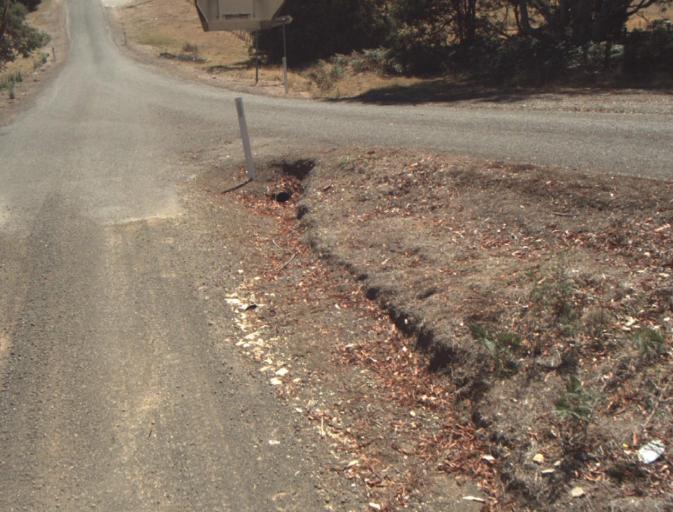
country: AU
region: Tasmania
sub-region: Dorset
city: Scottsdale
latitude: -41.2902
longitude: 147.3407
